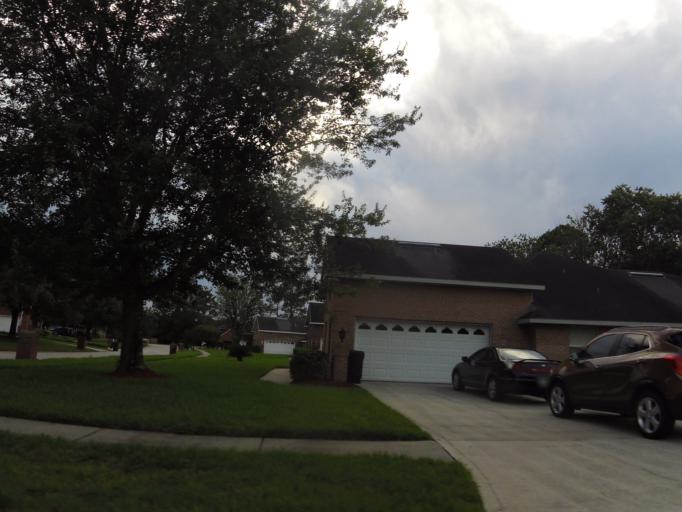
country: US
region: Florida
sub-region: Duval County
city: Baldwin
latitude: 30.3092
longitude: -81.8287
